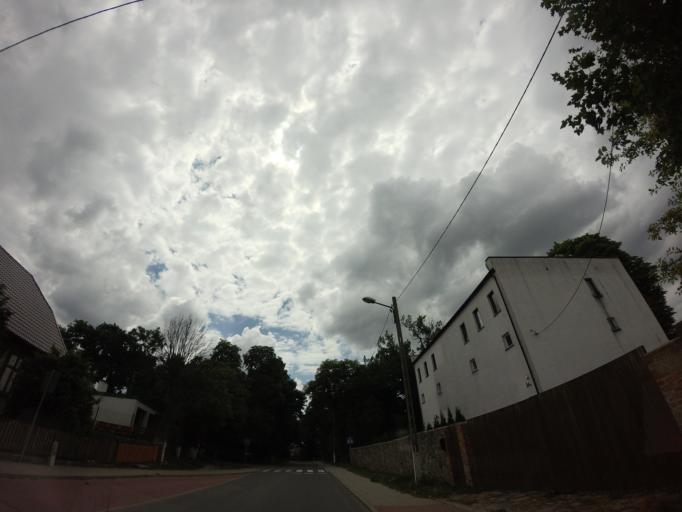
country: PL
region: West Pomeranian Voivodeship
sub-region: Powiat choszczenski
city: Choszczno
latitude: 53.1693
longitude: 15.4978
